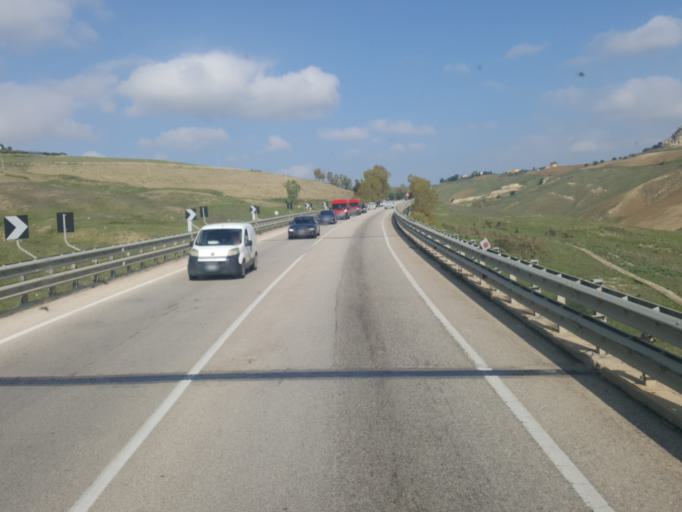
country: IT
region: Sicily
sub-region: Provincia di Caltanissetta
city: Caltanissetta
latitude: 37.4655
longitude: 14.0993
